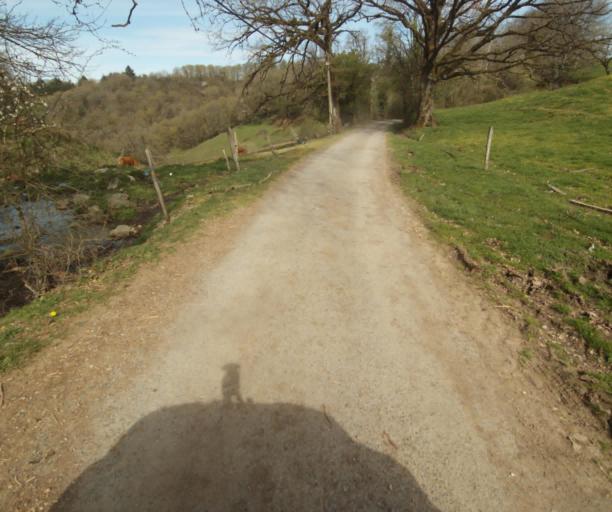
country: FR
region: Limousin
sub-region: Departement de la Correze
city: Correze
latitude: 45.3840
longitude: 1.8197
